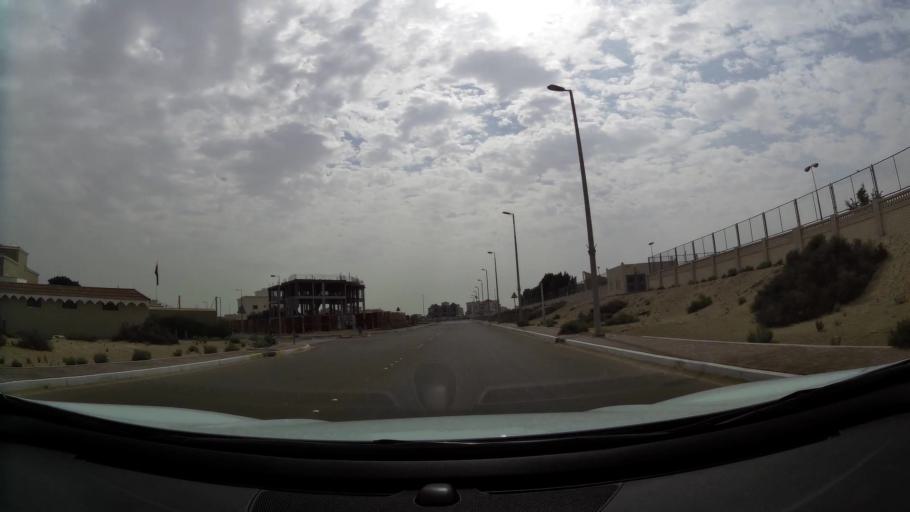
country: AE
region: Abu Dhabi
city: Abu Dhabi
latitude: 24.3157
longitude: 54.6447
